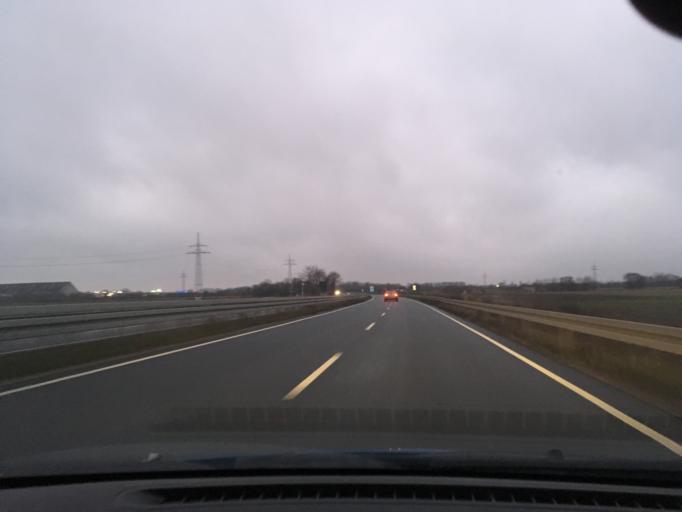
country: DE
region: Lower Saxony
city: Lehrte
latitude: 52.3584
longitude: 9.9016
